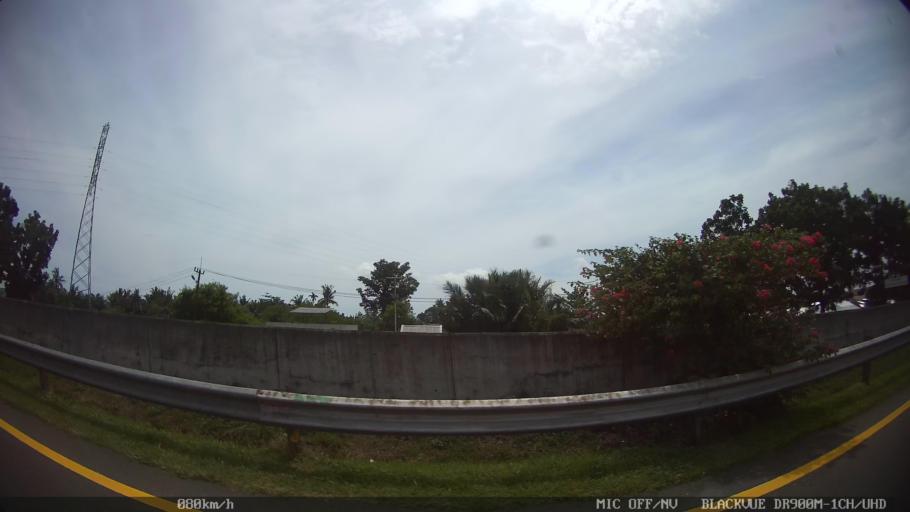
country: ID
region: North Sumatra
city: Labuhan Deli
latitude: 3.7203
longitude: 98.6828
